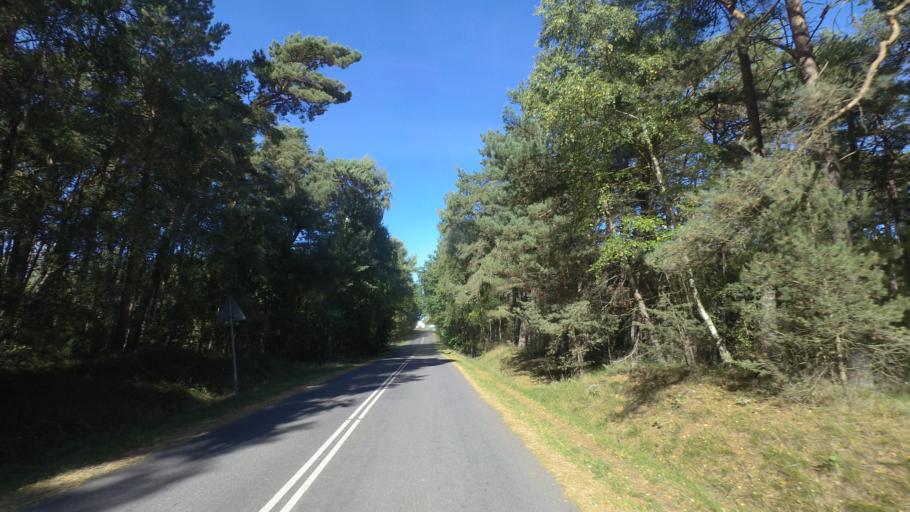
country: DK
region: Capital Region
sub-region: Bornholm Kommune
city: Nexo
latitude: 54.9998
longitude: 15.0755
